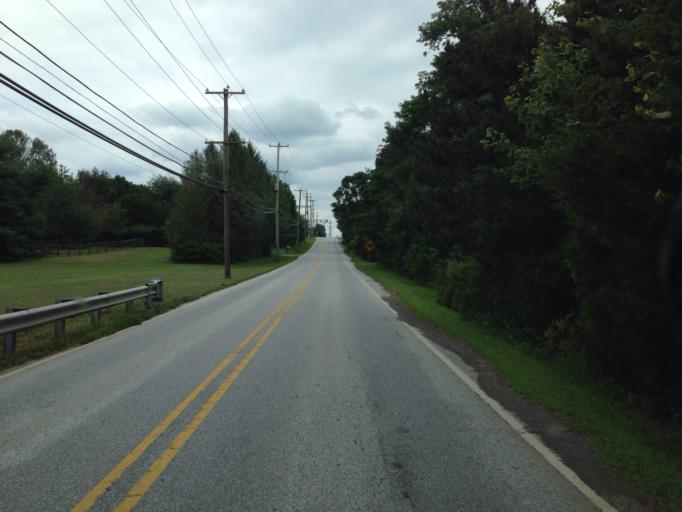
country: US
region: Pennsylvania
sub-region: Chester County
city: West Grove
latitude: 39.8103
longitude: -75.8962
